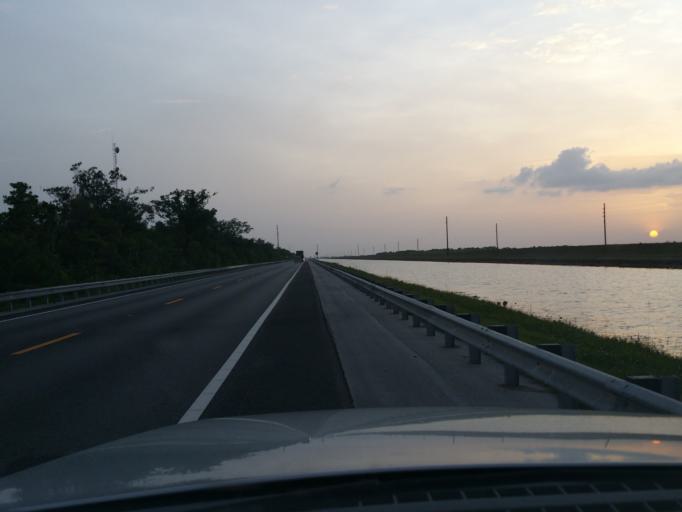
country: US
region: Florida
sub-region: Miami-Dade County
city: Kendall West
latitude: 25.7610
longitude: -80.6170
